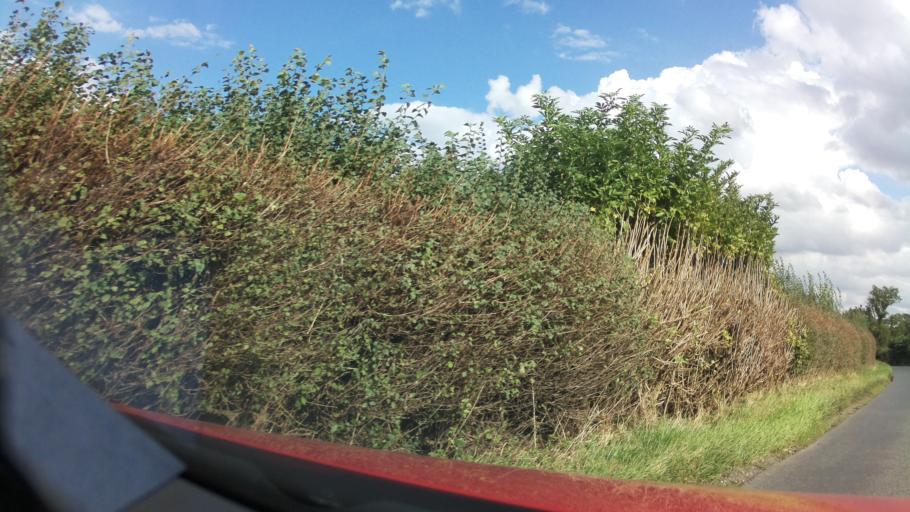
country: GB
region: England
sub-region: North Yorkshire
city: Leyburn
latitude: 54.2682
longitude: -1.7625
